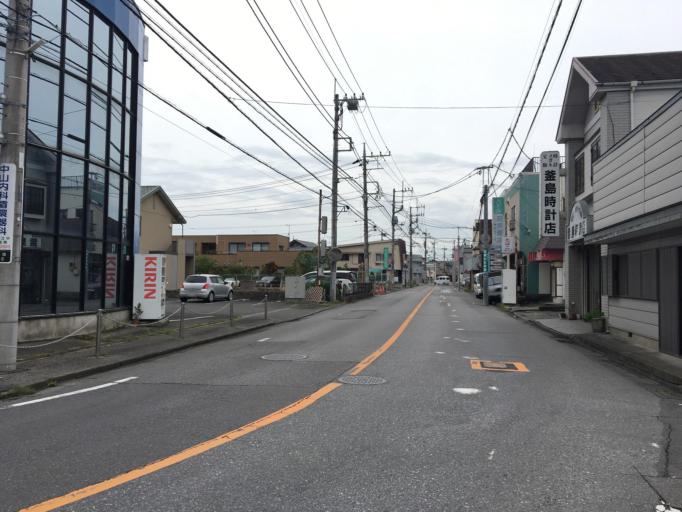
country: JP
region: Tochigi
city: Utsunomiya-shi
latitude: 36.5666
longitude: 139.8760
